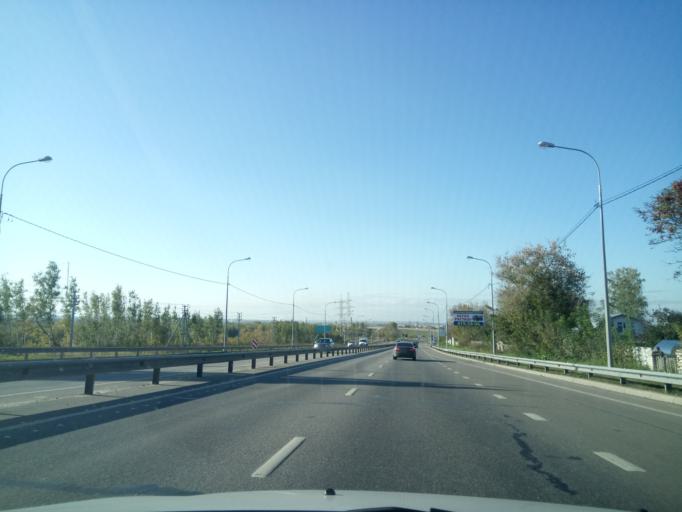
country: RU
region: Nizjnij Novgorod
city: Burevestnik
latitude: 56.1855
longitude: 43.9216
